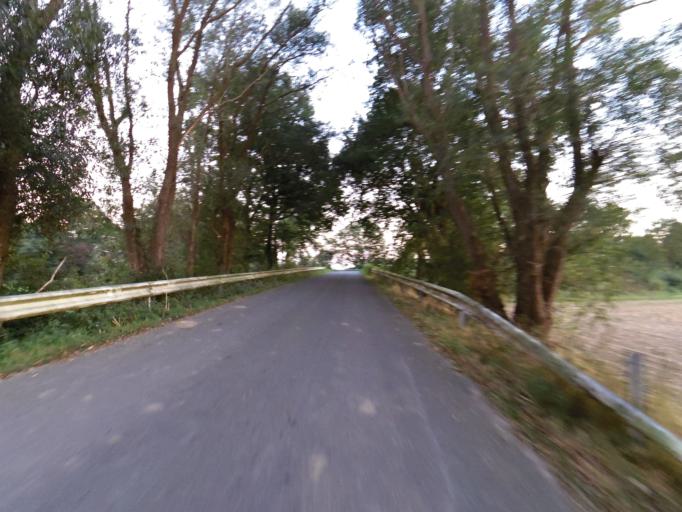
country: NL
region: Gelderland
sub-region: Gemeente Montferland
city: s-Heerenberg
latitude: 51.8518
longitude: 6.2964
